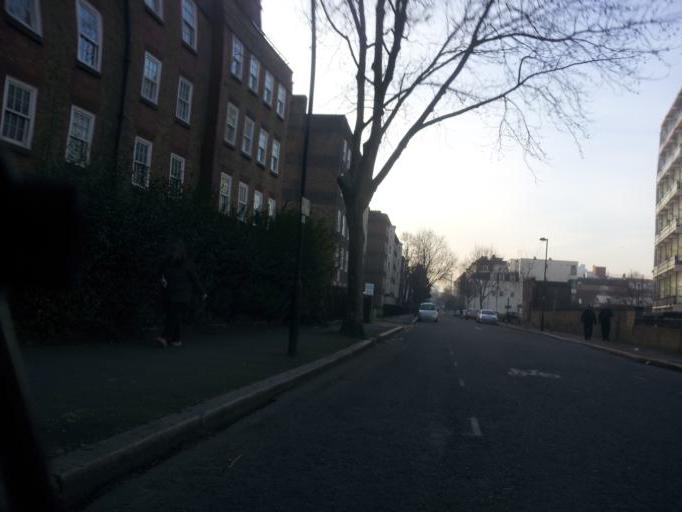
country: GB
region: England
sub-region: Greater London
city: Lambeth
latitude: 51.4911
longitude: -0.1181
